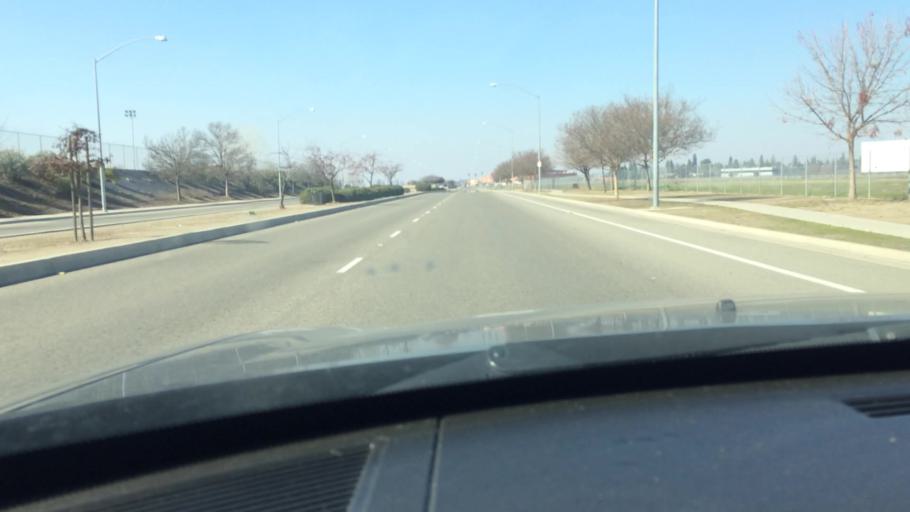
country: US
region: California
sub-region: Fresno County
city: Tarpey Village
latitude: 36.7809
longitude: -119.7119
